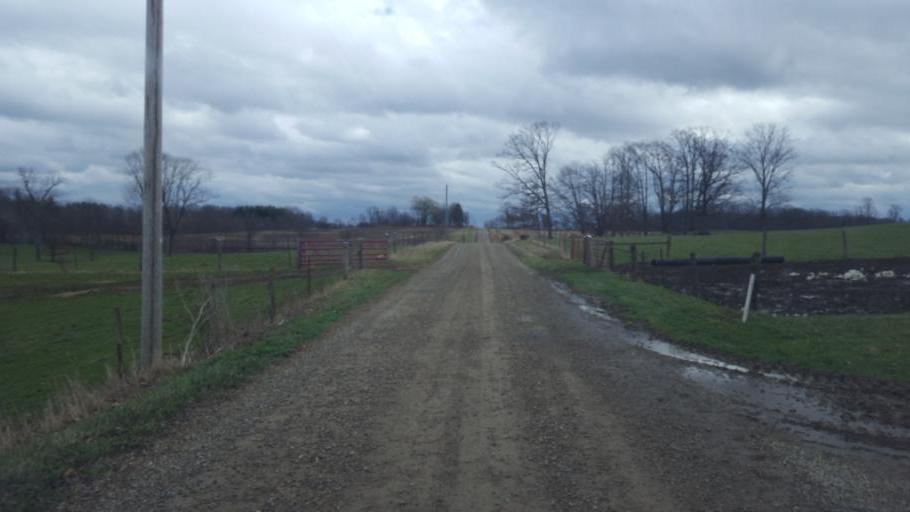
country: US
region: Ohio
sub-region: Knox County
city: Mount Vernon
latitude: 40.3344
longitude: -82.5574
